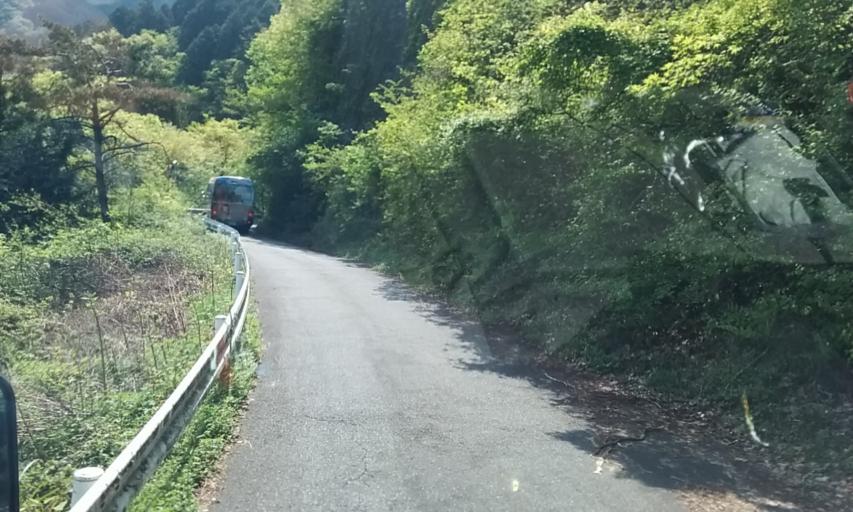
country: JP
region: Ehime
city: Niihama
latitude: 33.8747
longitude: 133.3032
